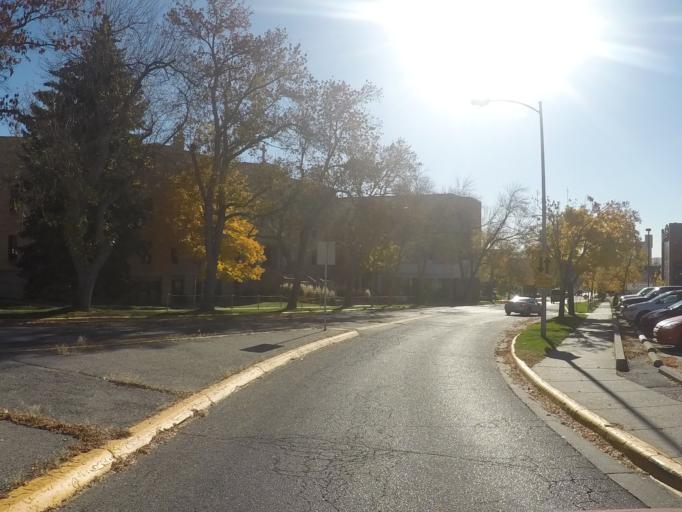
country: US
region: Montana
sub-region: Yellowstone County
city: Billings
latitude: 45.7938
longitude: -108.5211
